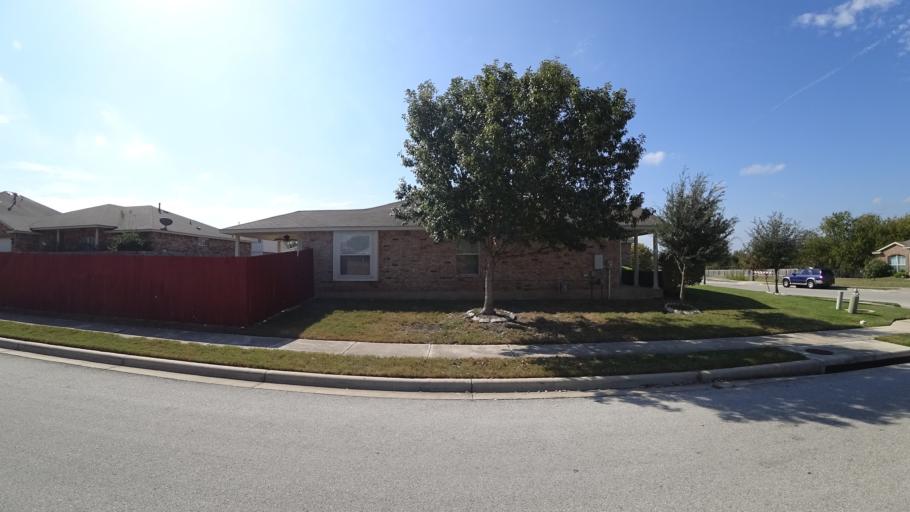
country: US
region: Texas
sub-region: Travis County
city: Pflugerville
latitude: 30.4201
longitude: -97.6367
